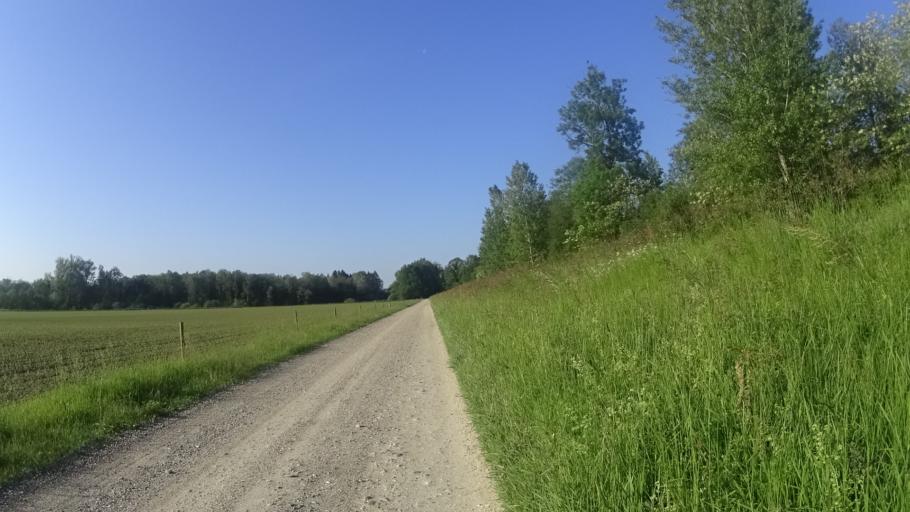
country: DE
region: Baden-Wuerttemberg
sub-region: Freiburg Region
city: Rheinau
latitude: 48.6965
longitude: 7.9518
